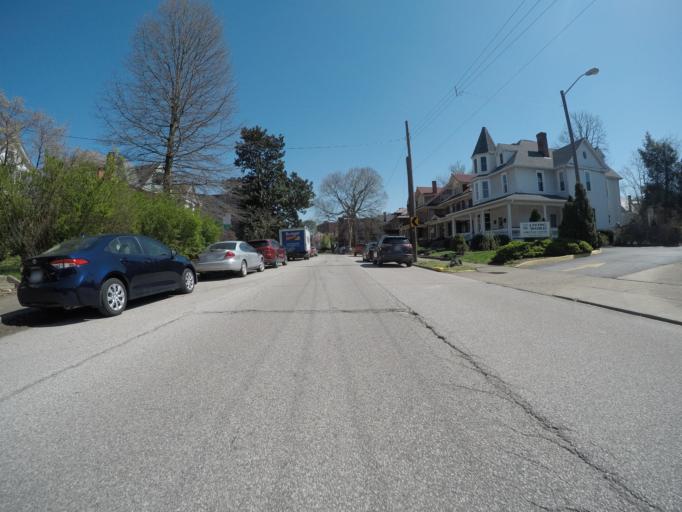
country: US
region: West Virginia
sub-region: Kanawha County
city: Charleston
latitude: 38.3421
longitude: -81.6266
